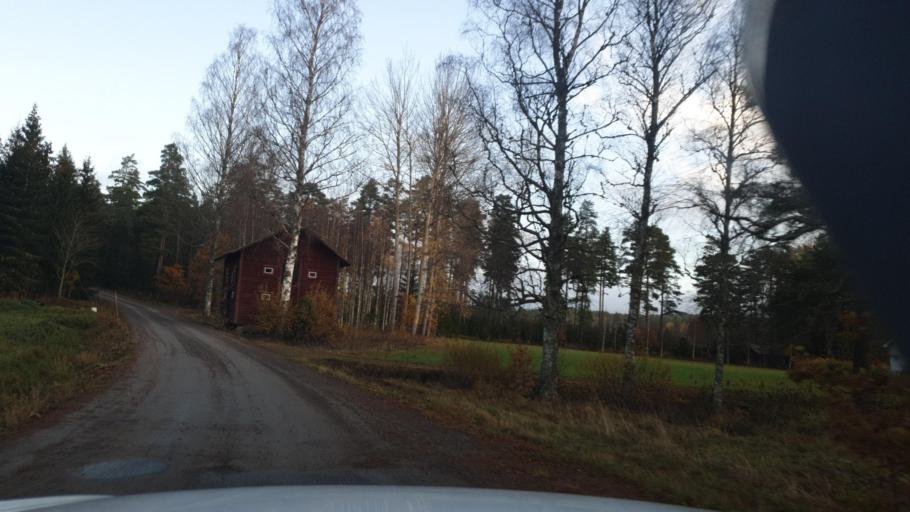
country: SE
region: Vaermland
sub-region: Arvika Kommun
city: Arvika
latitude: 59.5555
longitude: 12.7447
